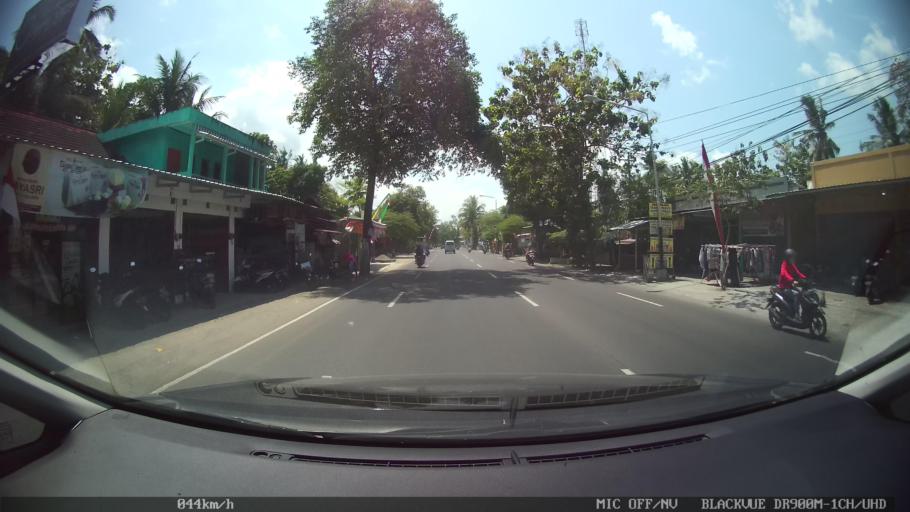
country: ID
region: Daerah Istimewa Yogyakarta
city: Bambanglipuro
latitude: -7.9299
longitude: 110.2738
